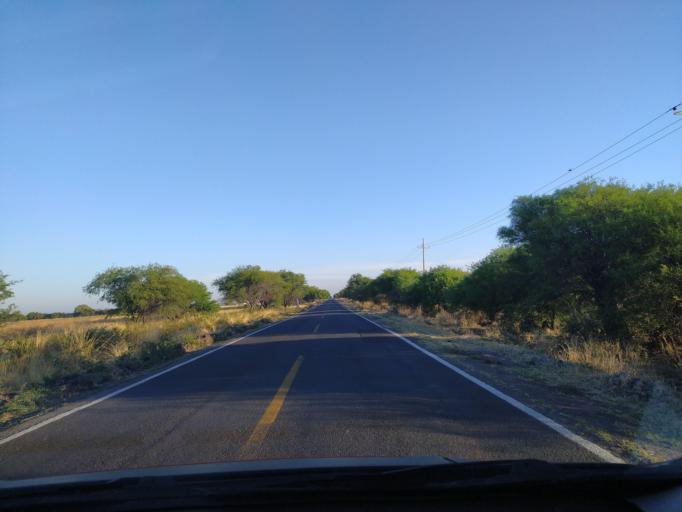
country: MX
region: Guanajuato
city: Ciudad Manuel Doblado
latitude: 20.7560
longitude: -101.8265
